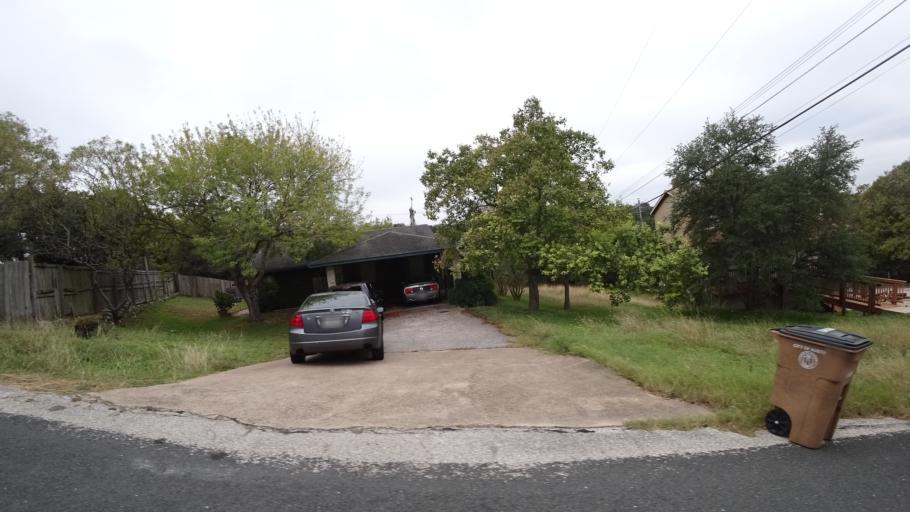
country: US
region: Texas
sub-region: Travis County
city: Barton Creek
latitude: 30.2424
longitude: -97.8886
